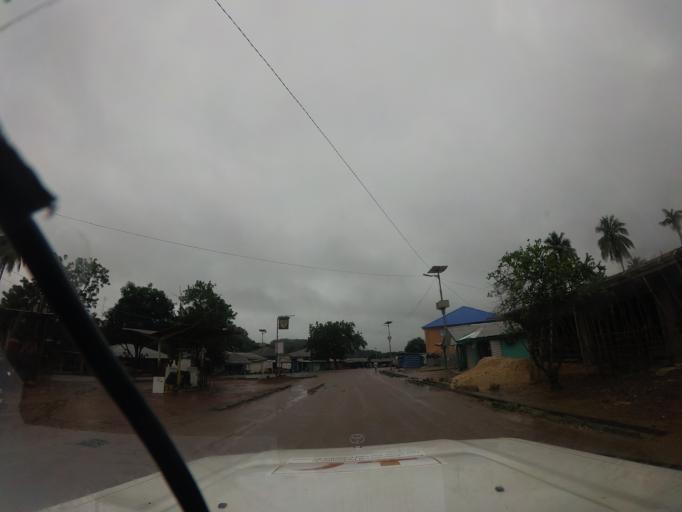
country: SL
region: Northern Province
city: Kabala
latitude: 9.5828
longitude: -11.5535
